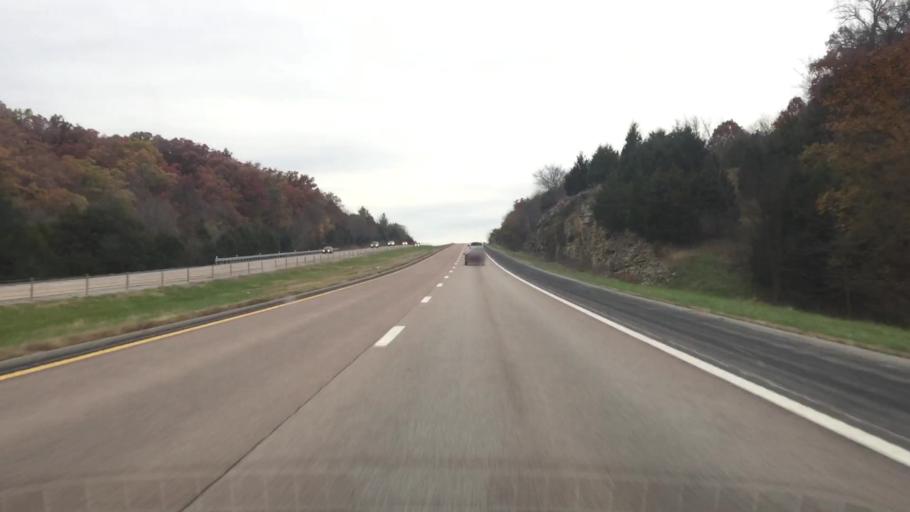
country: US
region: Missouri
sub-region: Boone County
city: Ashland
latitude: 38.6889
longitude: -92.2550
